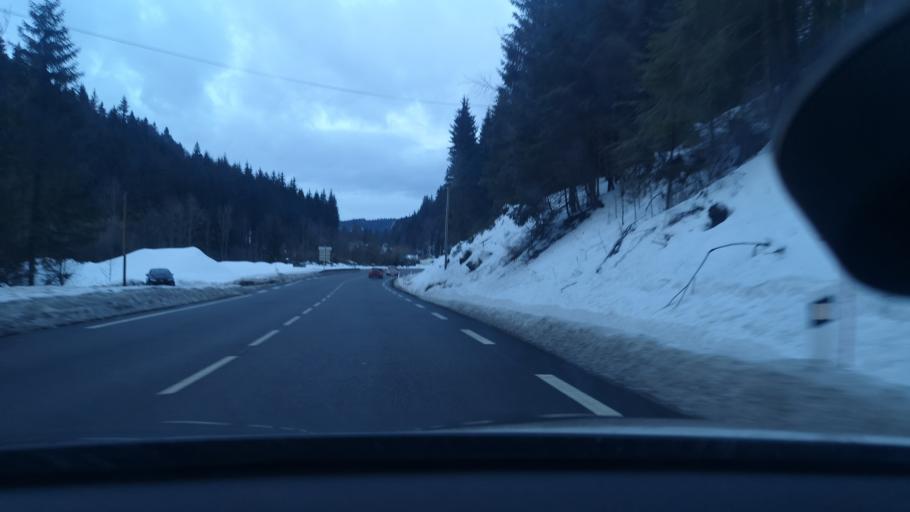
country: FR
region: Franche-Comte
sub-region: Departement du Doubs
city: Les Fourgs
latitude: 46.8463
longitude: 6.3705
